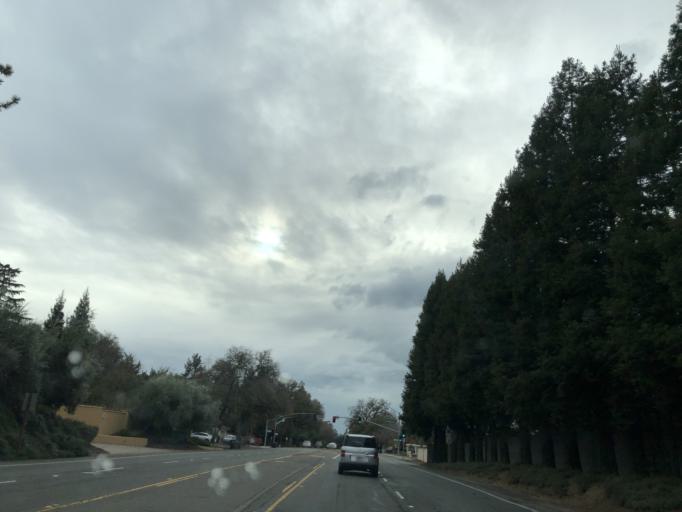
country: US
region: California
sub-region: Sacramento County
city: Carmichael
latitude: 38.6051
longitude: -121.3356
